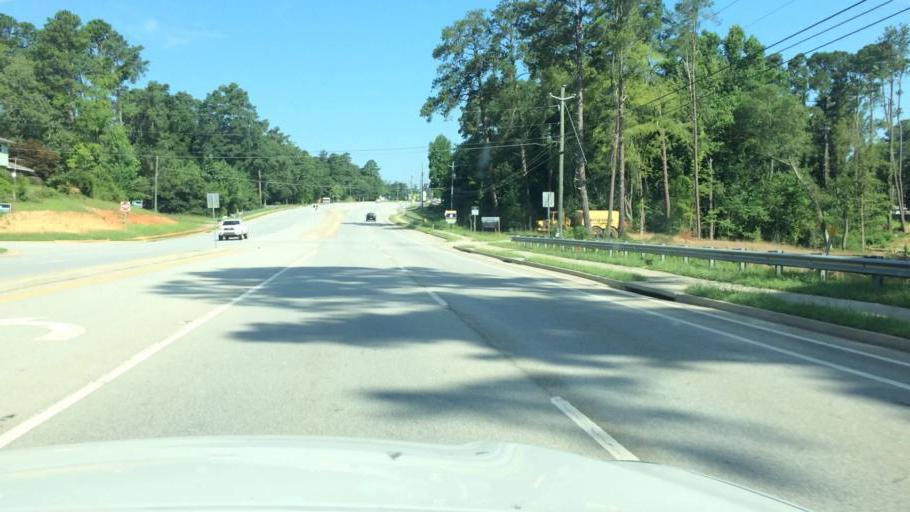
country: US
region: Georgia
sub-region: Columbia County
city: Martinez
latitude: 33.5225
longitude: -82.0662
